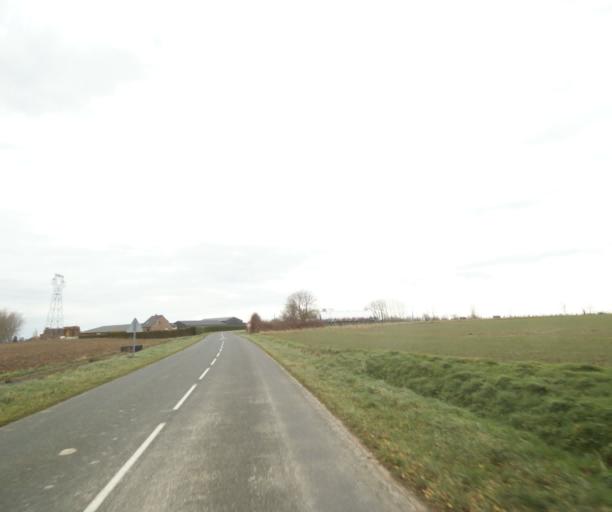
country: FR
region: Nord-Pas-de-Calais
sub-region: Departement du Nord
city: Sebourg
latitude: 50.3375
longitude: 3.6333
